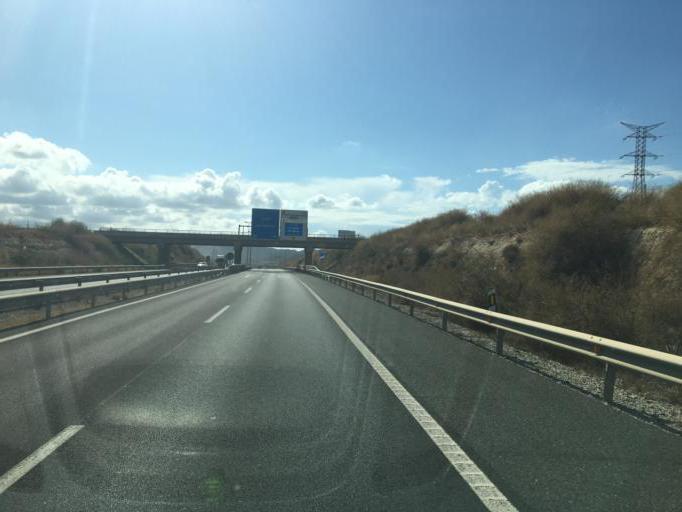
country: ES
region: Murcia
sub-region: Murcia
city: Cartagena
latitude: 37.6315
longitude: -0.9529
